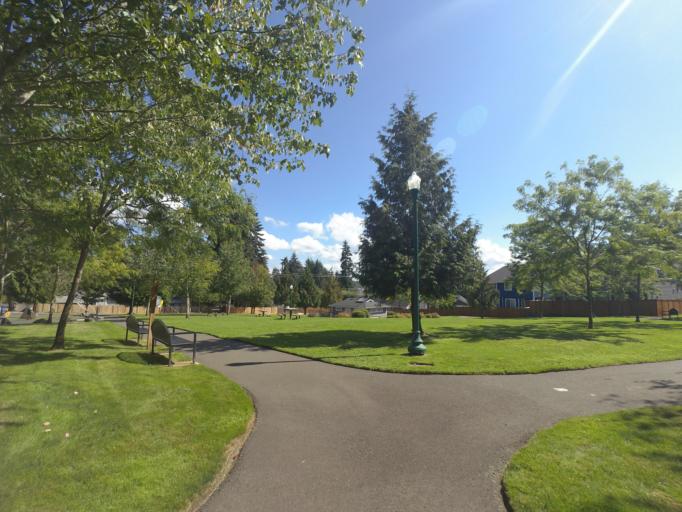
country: US
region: Washington
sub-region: Pierce County
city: Fircrest
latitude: 47.2191
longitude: -122.5167
